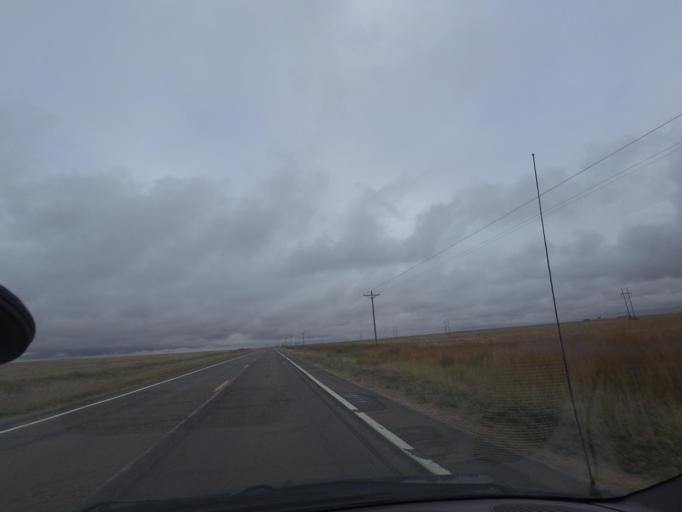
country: US
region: Colorado
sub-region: Washington County
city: Akron
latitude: 39.7416
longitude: -103.1891
